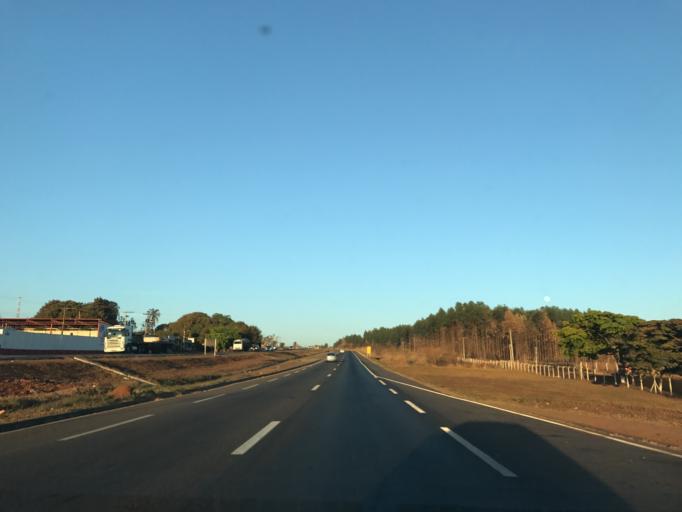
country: BR
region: Goias
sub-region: Anapolis
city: Anapolis
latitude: -16.3007
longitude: -48.8132
